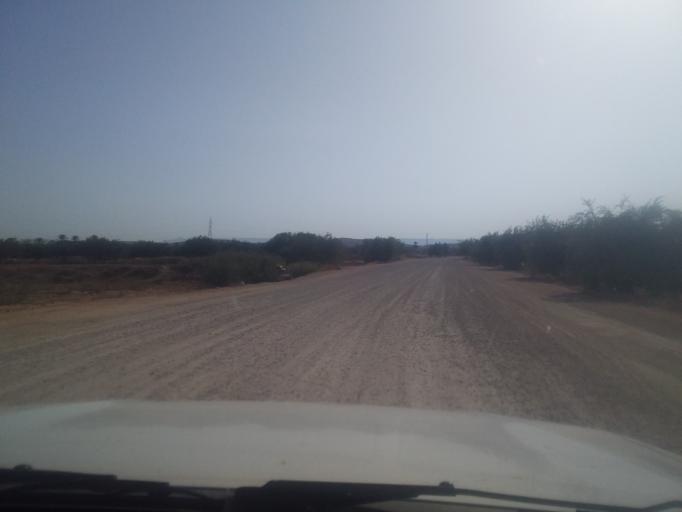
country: TN
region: Qabis
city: Matmata
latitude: 33.5931
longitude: 10.2721
